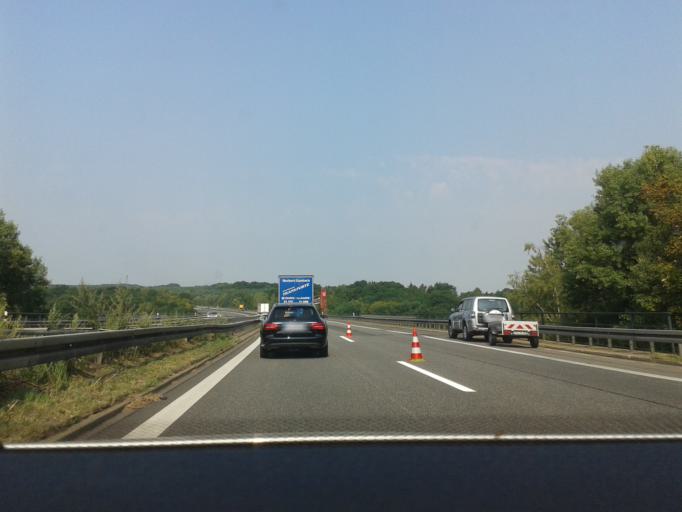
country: DE
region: Saxony
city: Nerchau
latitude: 51.2570
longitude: 12.7849
